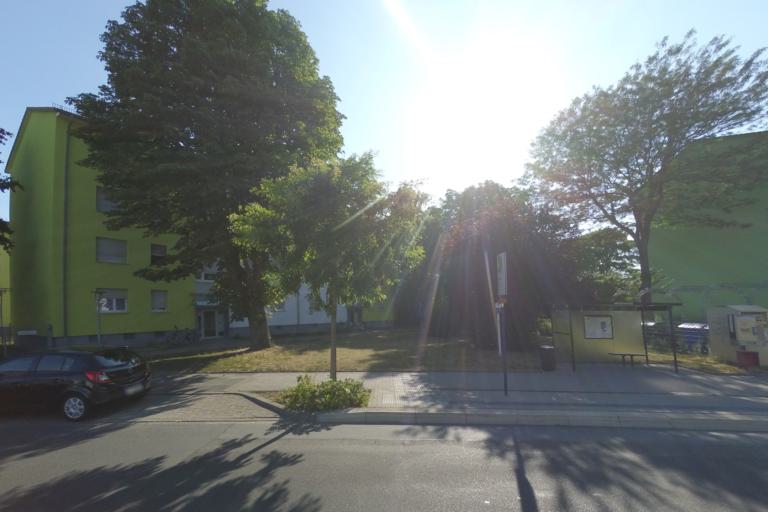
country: DE
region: Rheinland-Pfalz
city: Gartenstadt
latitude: 49.4677
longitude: 8.4074
